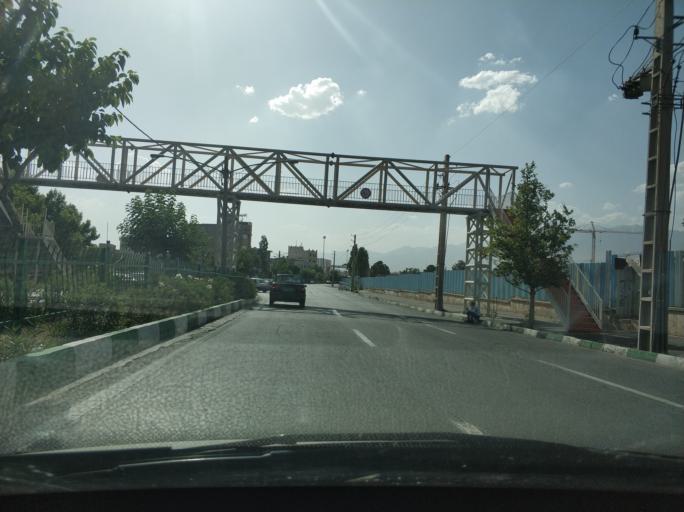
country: IR
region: Tehran
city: Tajrish
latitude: 35.7458
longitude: 51.5737
